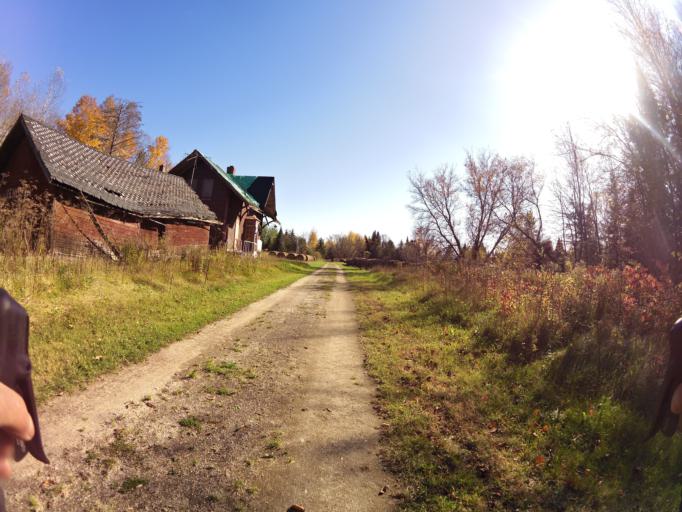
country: CA
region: Quebec
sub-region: Outaouais
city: Wakefield
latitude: 45.8691
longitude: -76.0240
